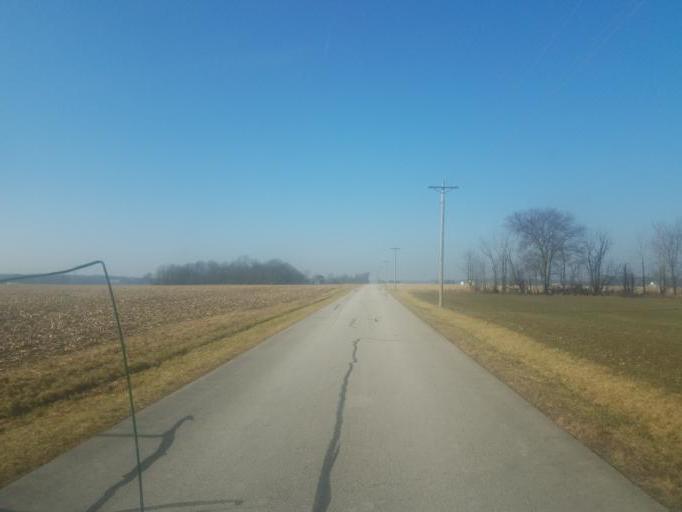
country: US
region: Ohio
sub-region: Seneca County
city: Tiffin
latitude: 41.0371
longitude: -83.1036
